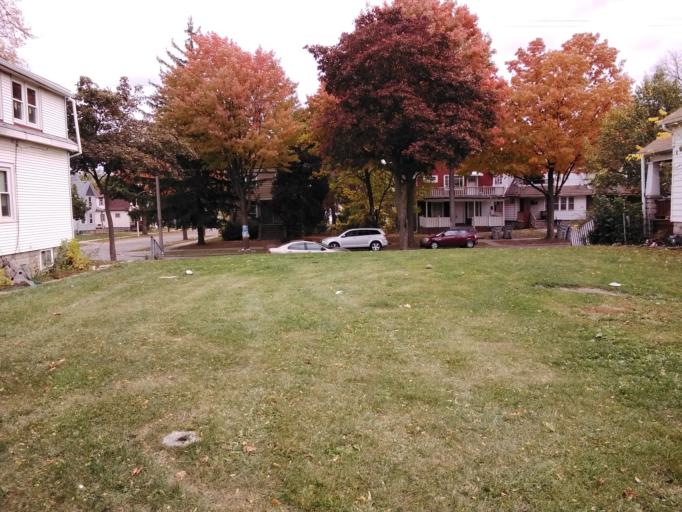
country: US
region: Wisconsin
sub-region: Milwaukee County
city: Glendale
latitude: 43.1105
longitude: -87.9520
